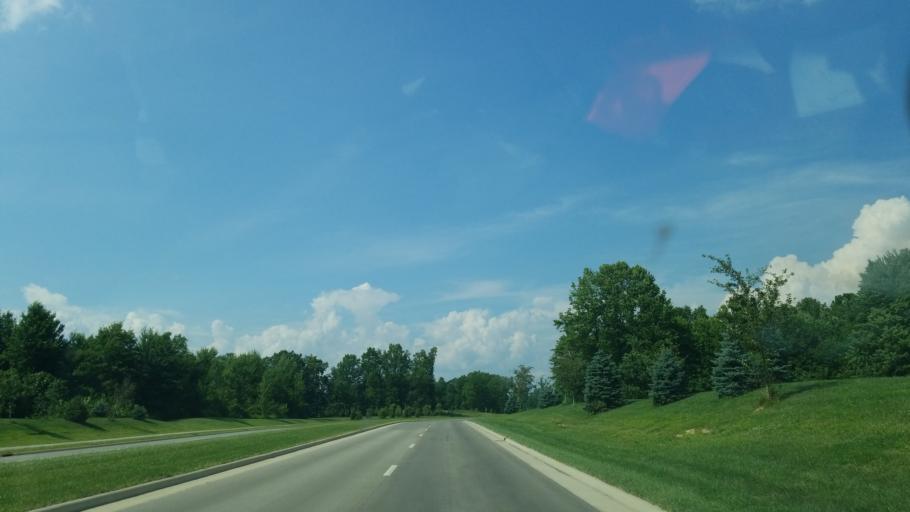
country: US
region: Ohio
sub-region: Delaware County
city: Delaware
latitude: 40.2466
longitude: -83.0931
